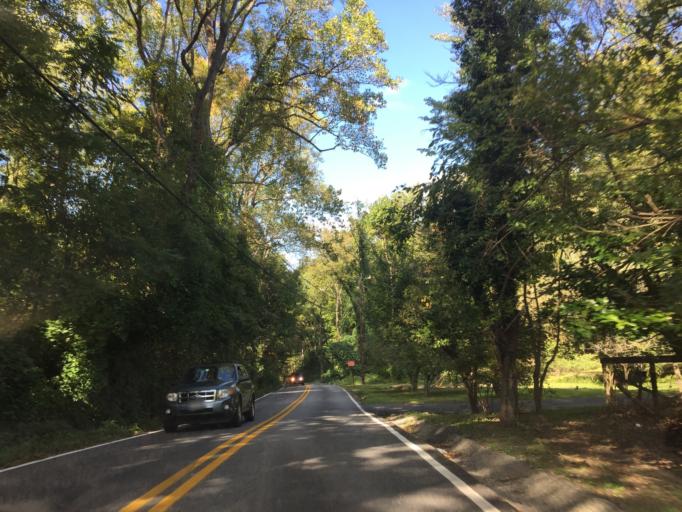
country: US
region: Maryland
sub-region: Baltimore County
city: Carney
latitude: 39.4137
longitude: -76.5398
